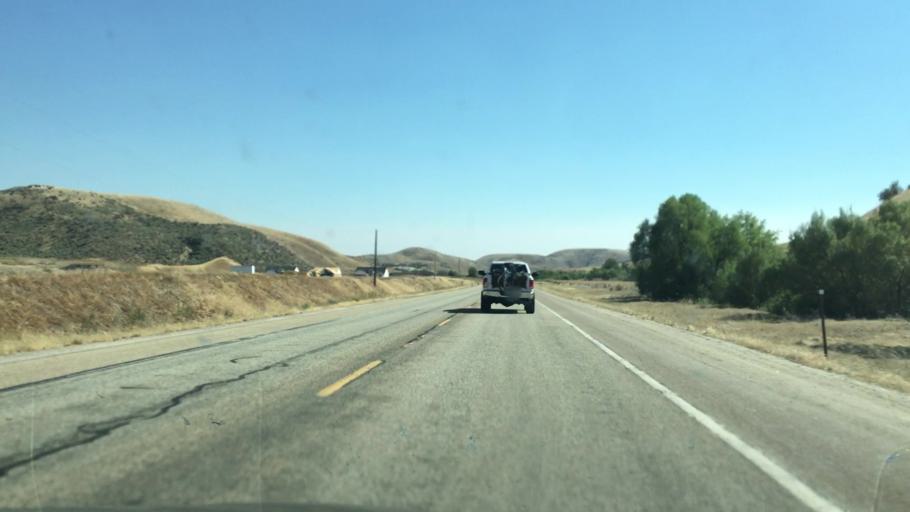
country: US
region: Idaho
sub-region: Ada County
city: Eagle
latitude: 43.7915
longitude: -116.2632
